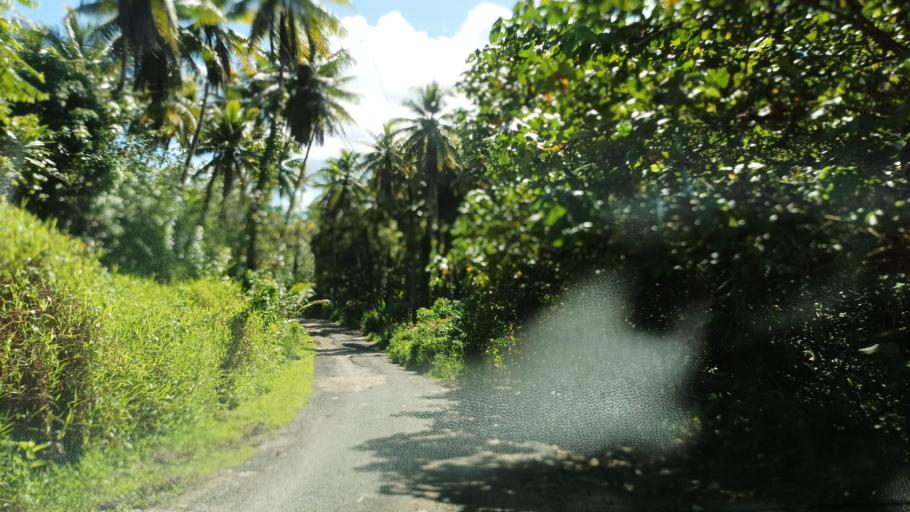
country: FM
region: Pohnpei
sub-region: Madolenihm Municipality
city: Madolenihm Municipality Government
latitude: 6.8490
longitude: 158.3178
